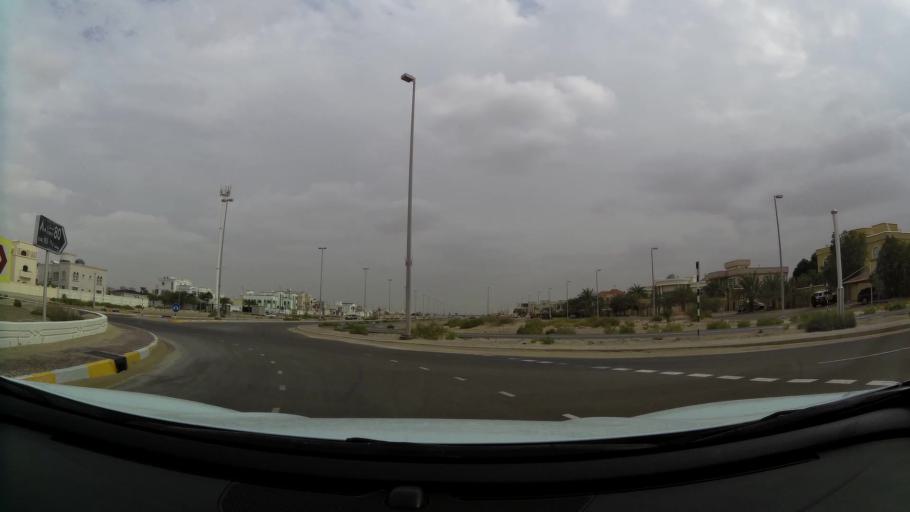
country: AE
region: Abu Dhabi
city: Abu Dhabi
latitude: 24.3890
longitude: 54.6405
